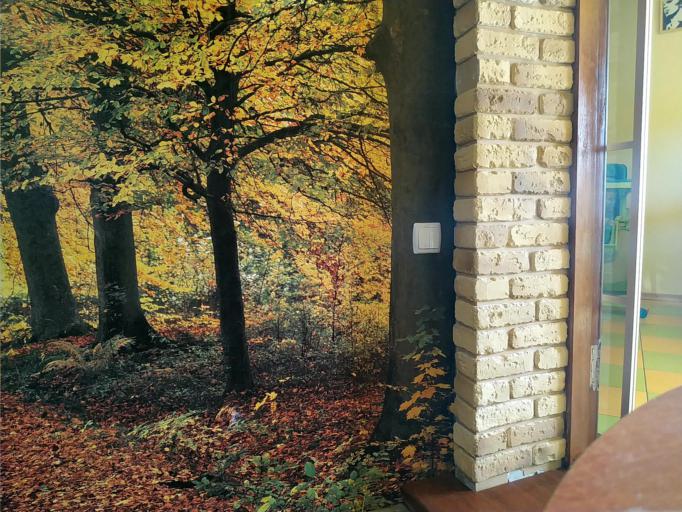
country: RU
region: Smolensk
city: Katyn'
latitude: 54.9945
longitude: 31.7488
